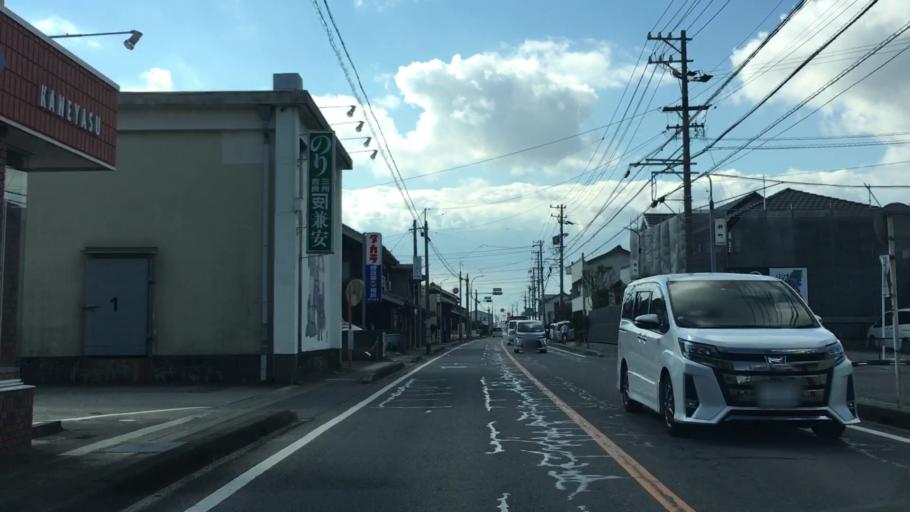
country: JP
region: Aichi
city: Ishiki
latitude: 34.7956
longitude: 137.0645
